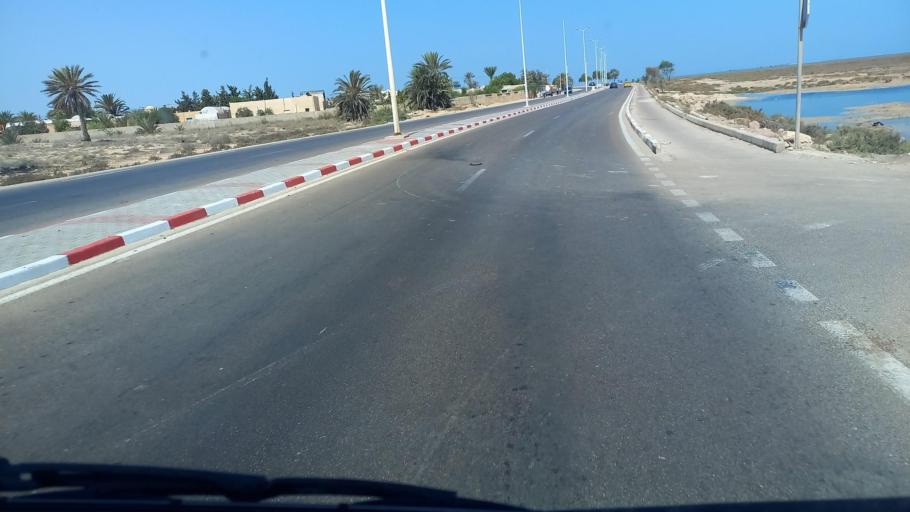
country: TN
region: Madanin
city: Houmt Souk
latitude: 33.8701
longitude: 10.9377
